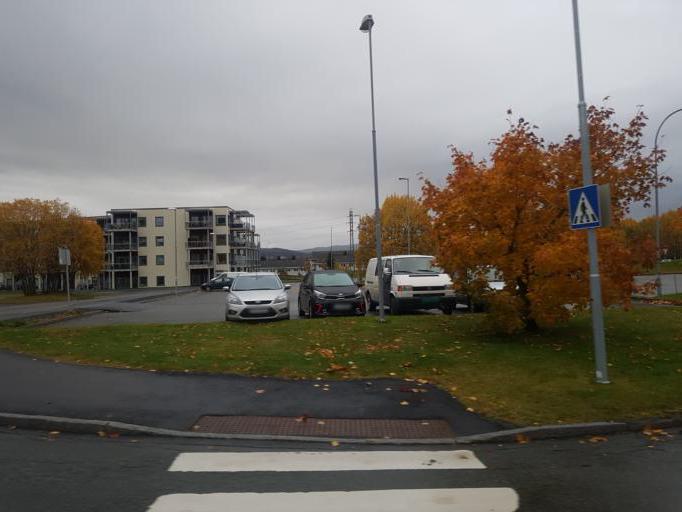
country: NO
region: Sor-Trondelag
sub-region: Trondheim
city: Trondheim
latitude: 63.3733
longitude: 10.3455
